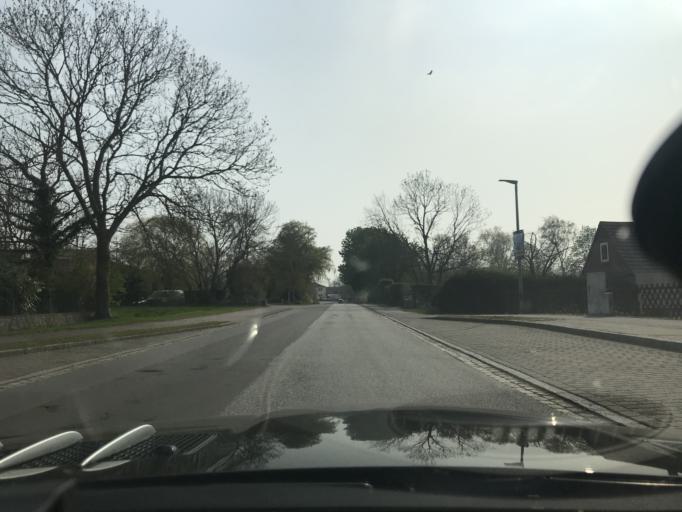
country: DE
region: Schleswig-Holstein
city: Fehmarn
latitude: 54.4953
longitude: 11.2118
